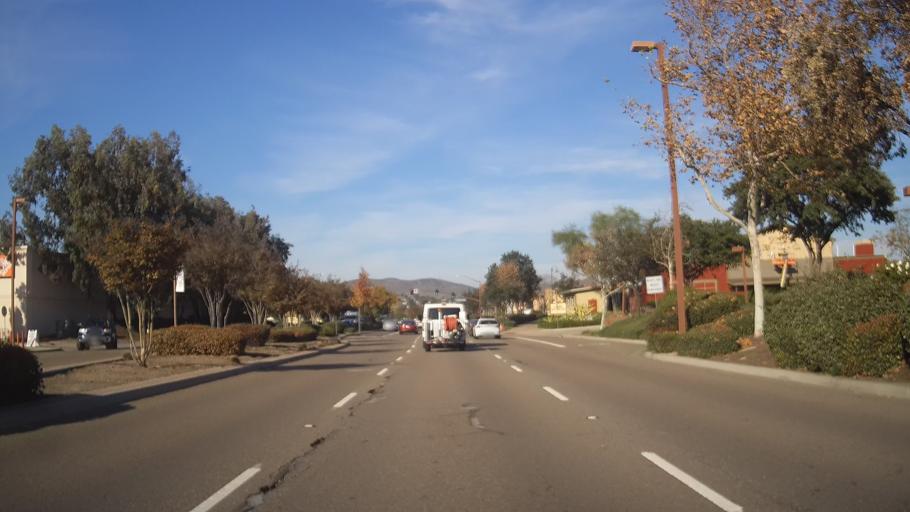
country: US
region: California
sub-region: San Diego County
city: Santee
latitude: 32.8396
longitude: -116.9837
